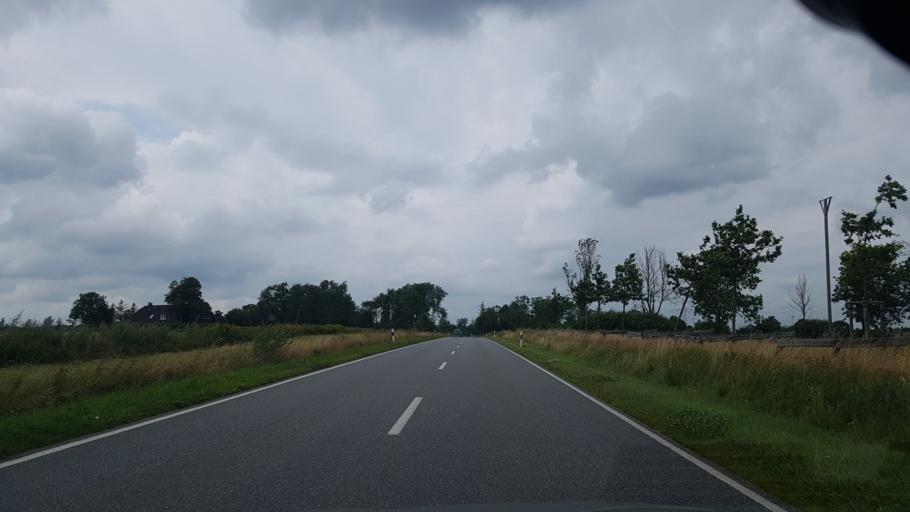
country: DE
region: Schleswig-Holstein
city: Osterby
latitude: 54.8150
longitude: 9.2287
